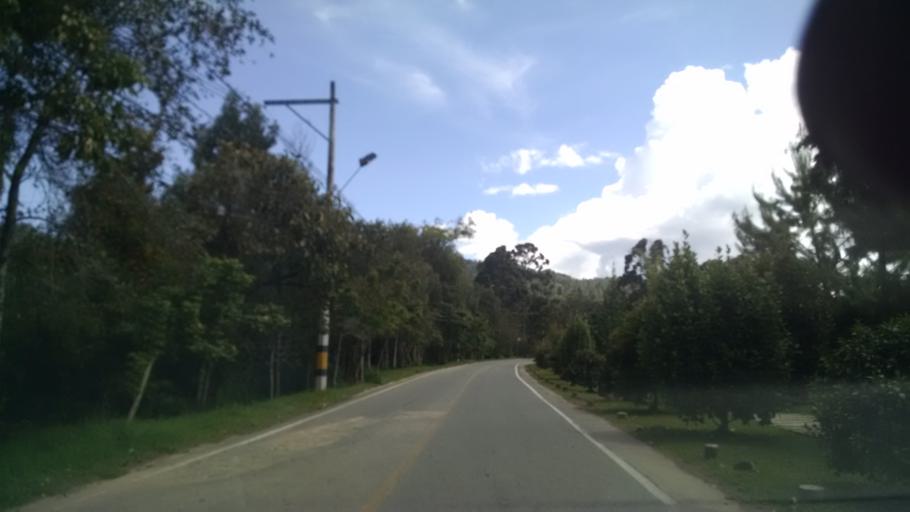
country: CO
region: Antioquia
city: El Retiro
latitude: 6.0757
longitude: -75.4983
